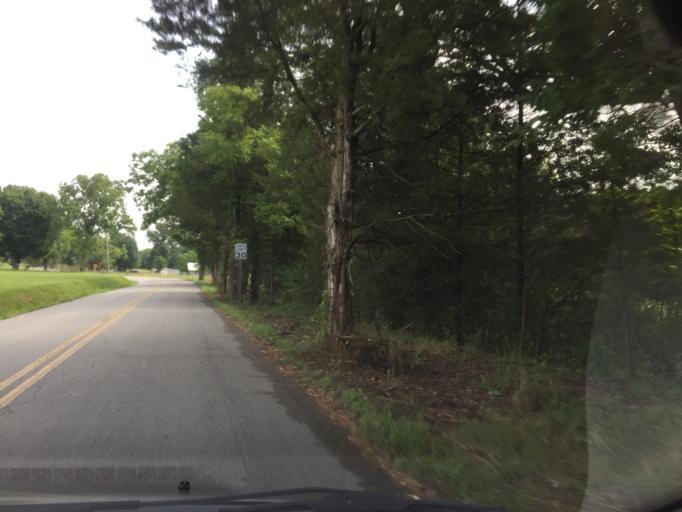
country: US
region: Tennessee
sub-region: Hamilton County
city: Collegedale
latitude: 35.0319
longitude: -85.0501
